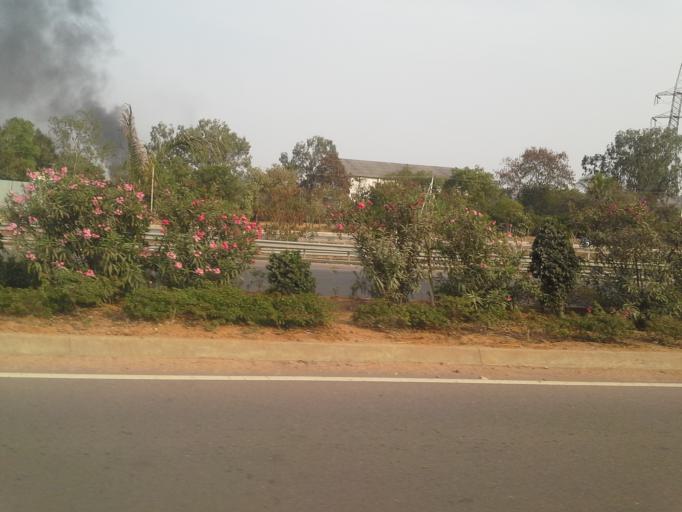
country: IN
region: Telangana
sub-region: Rangareddi
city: Kukatpalli
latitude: 17.4163
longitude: 78.3556
